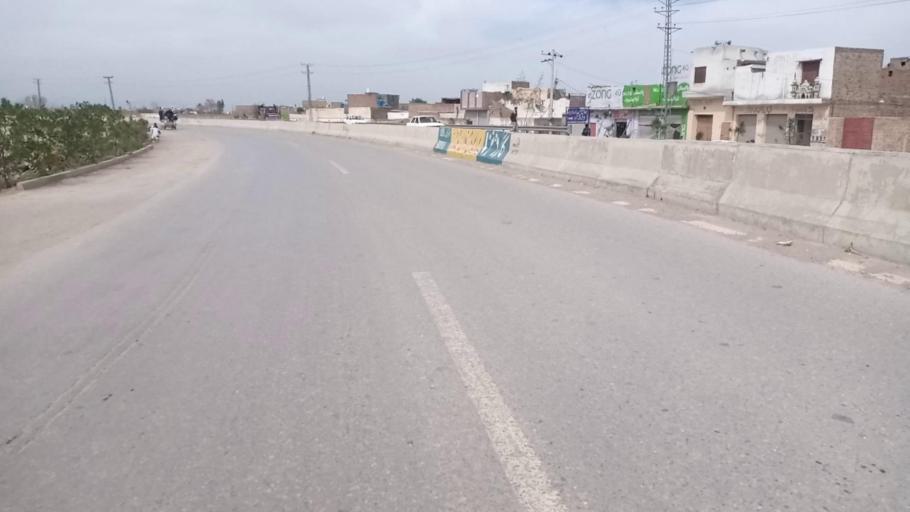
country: PK
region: Khyber Pakhtunkhwa
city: Peshawar
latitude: 34.0335
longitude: 71.6422
